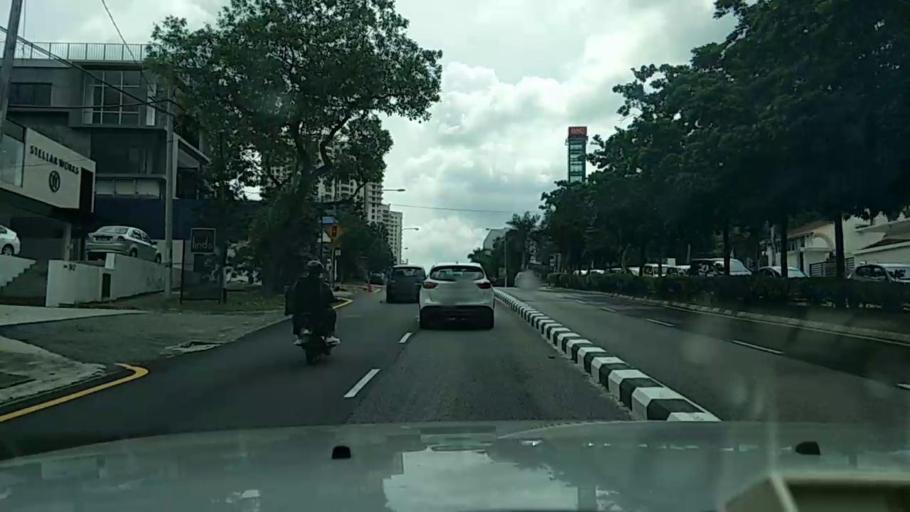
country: MY
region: Kuala Lumpur
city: Kuala Lumpur
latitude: 3.1425
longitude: 101.6690
